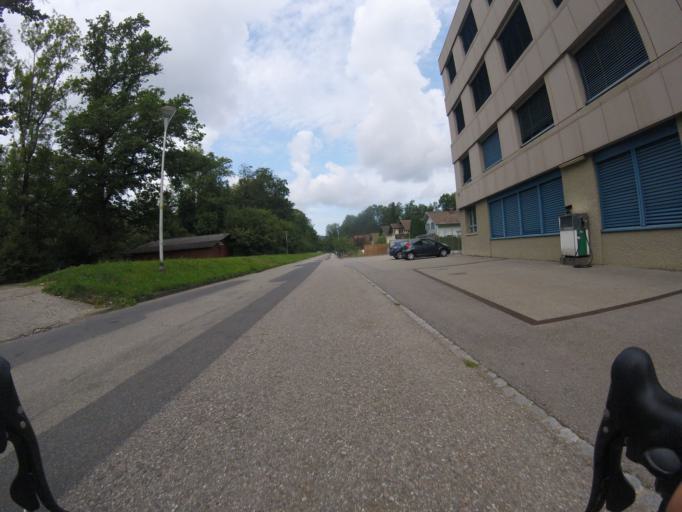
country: CH
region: Bern
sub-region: Emmental District
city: Oberburg
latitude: 47.0196
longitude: 7.6535
